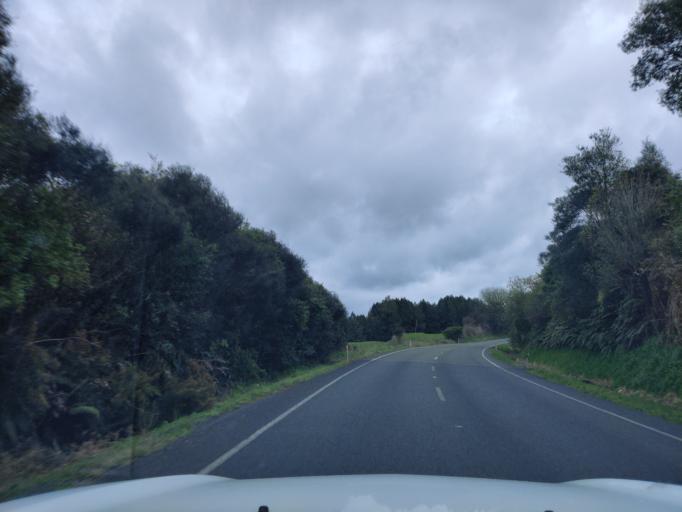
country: NZ
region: Waikato
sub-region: Otorohanga District
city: Otorohanga
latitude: -38.5494
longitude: 175.1871
